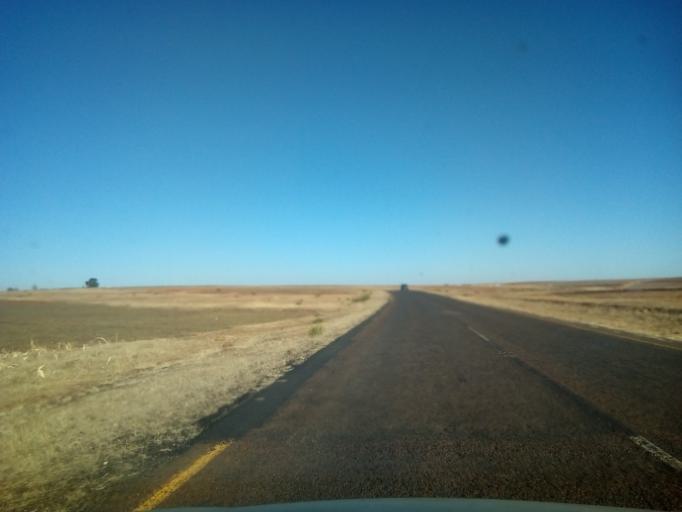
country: LS
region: Berea
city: Teyateyaneng
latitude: -29.2818
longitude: 27.6679
